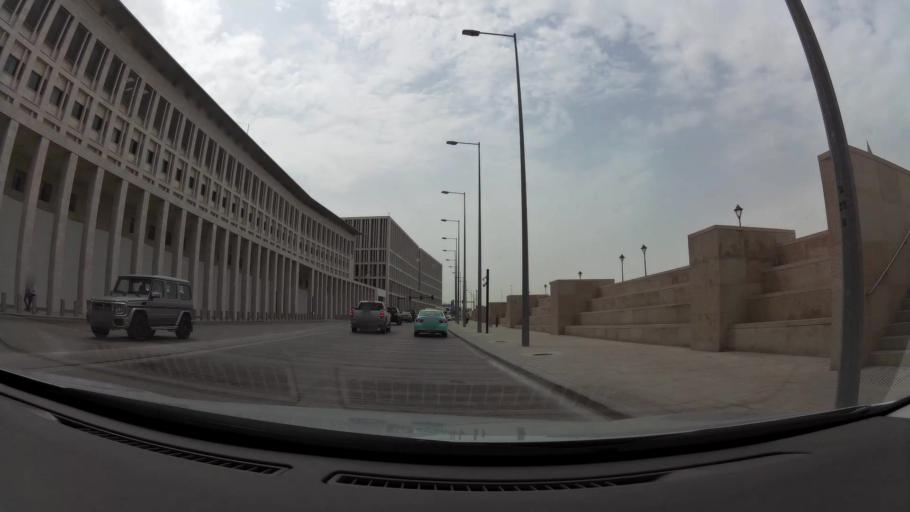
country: QA
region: Baladiyat ad Dawhah
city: Doha
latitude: 25.2882
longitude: 51.5295
